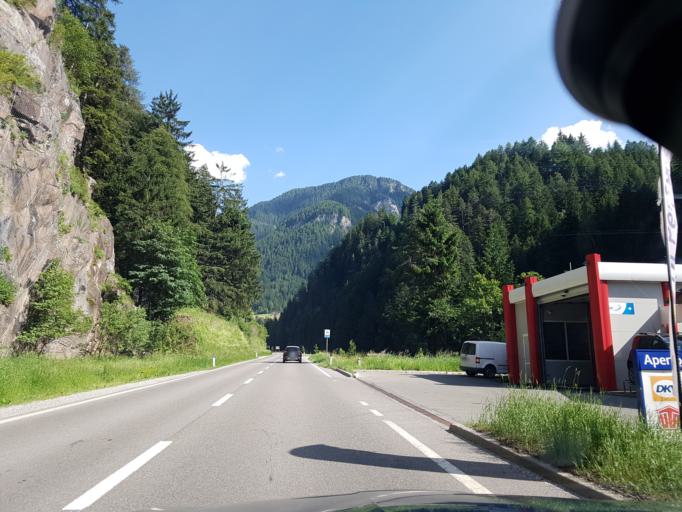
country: IT
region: Trentino-Alto Adige
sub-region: Bolzano
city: Ortisei
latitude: 46.5803
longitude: 11.6398
